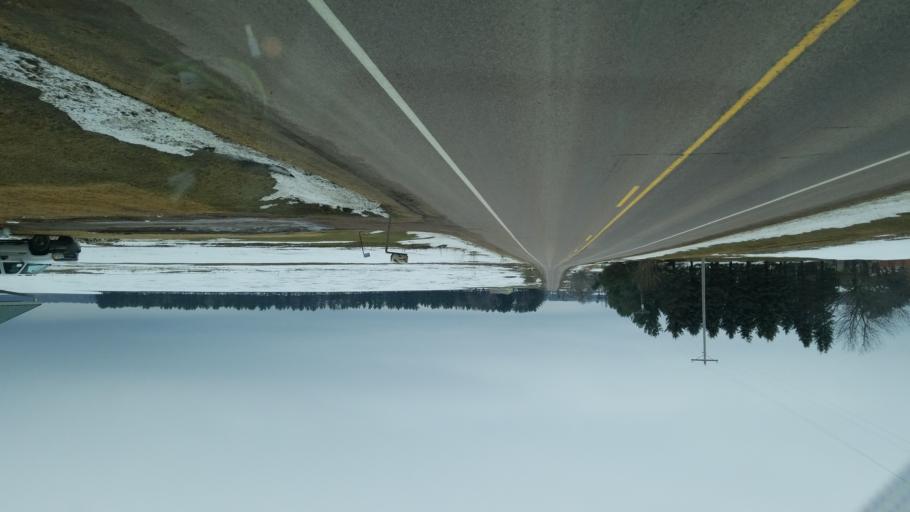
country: US
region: Wisconsin
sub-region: Wood County
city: Marshfield
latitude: 44.6434
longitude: -90.2184
